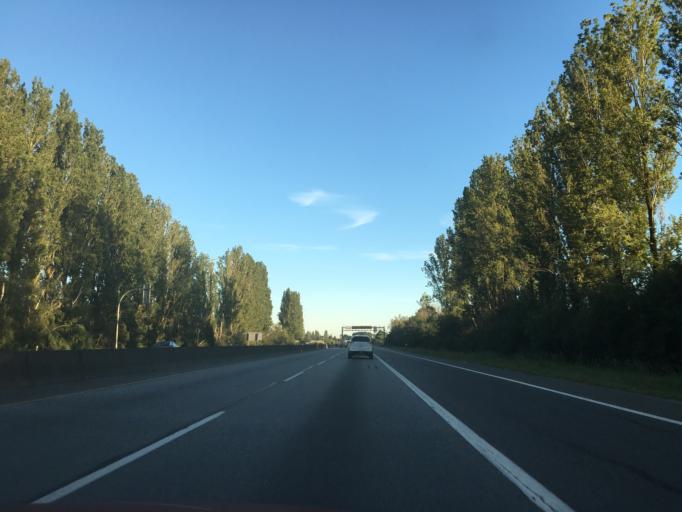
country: CA
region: British Columbia
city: Ladner
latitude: 49.1440
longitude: -123.0869
